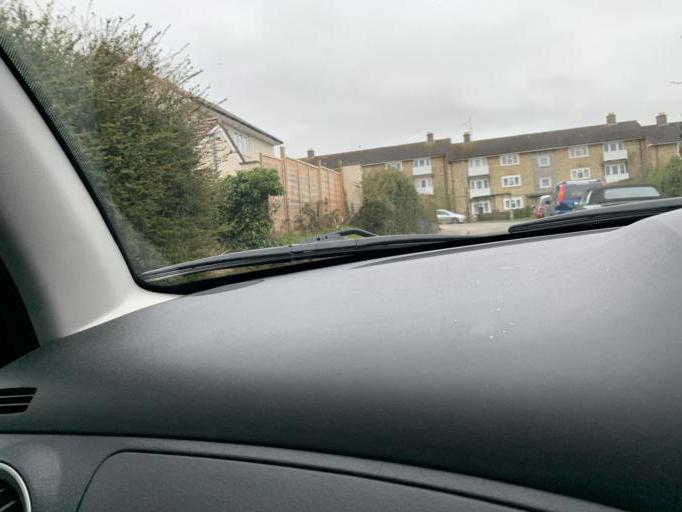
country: GB
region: England
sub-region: Wiltshire
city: Amesbury
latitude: 51.1726
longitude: -1.7743
